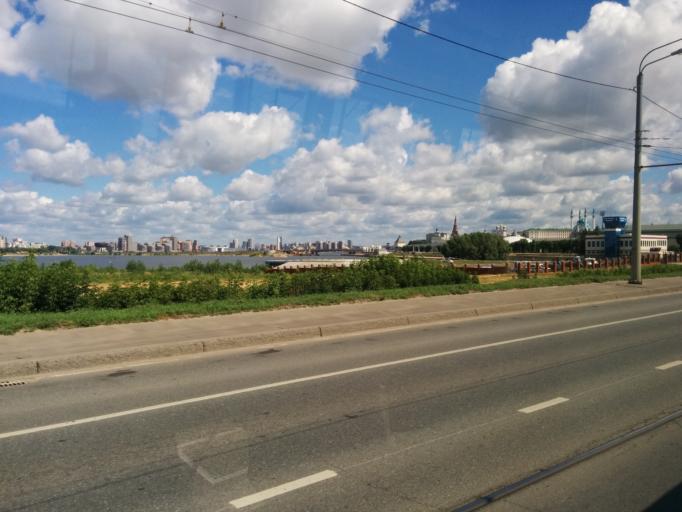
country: RU
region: Tatarstan
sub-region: Gorod Kazan'
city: Kazan
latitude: 55.7965
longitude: 49.0874
